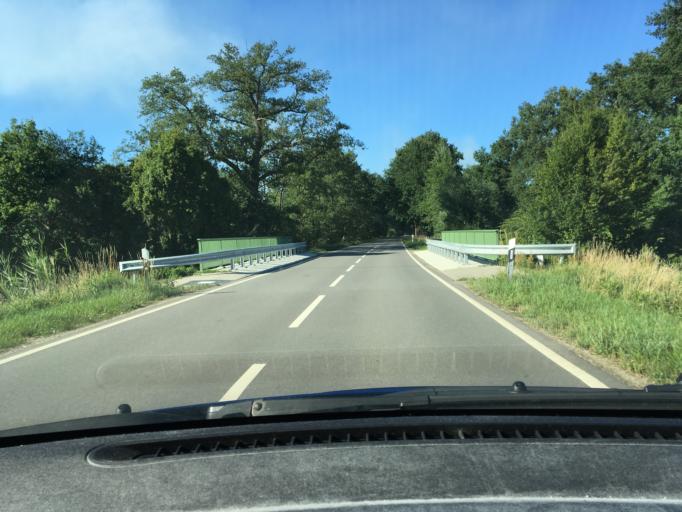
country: DE
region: Lower Saxony
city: Bleckede
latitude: 53.3270
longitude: 10.6760
